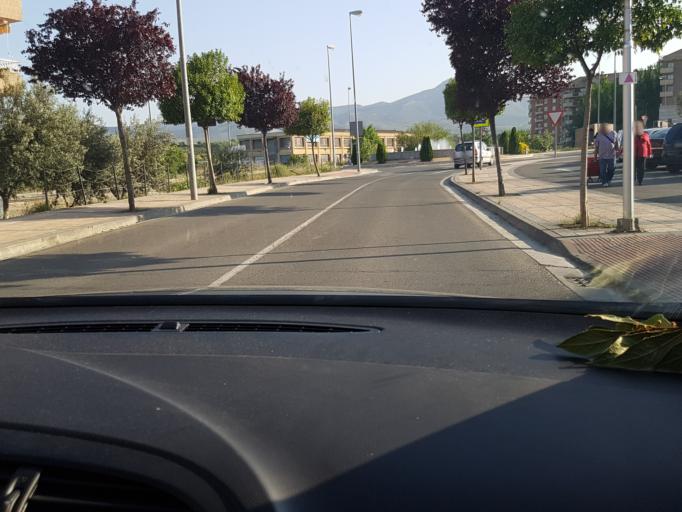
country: ES
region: La Rioja
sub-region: Provincia de La Rioja
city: Arnedo
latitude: 42.2279
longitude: -2.0935
